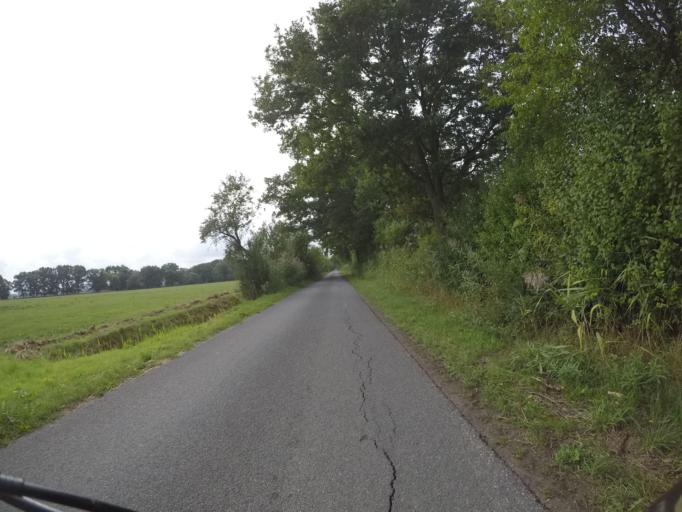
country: DE
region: Lower Saxony
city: Neu Darchau
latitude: 53.2845
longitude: 10.8439
